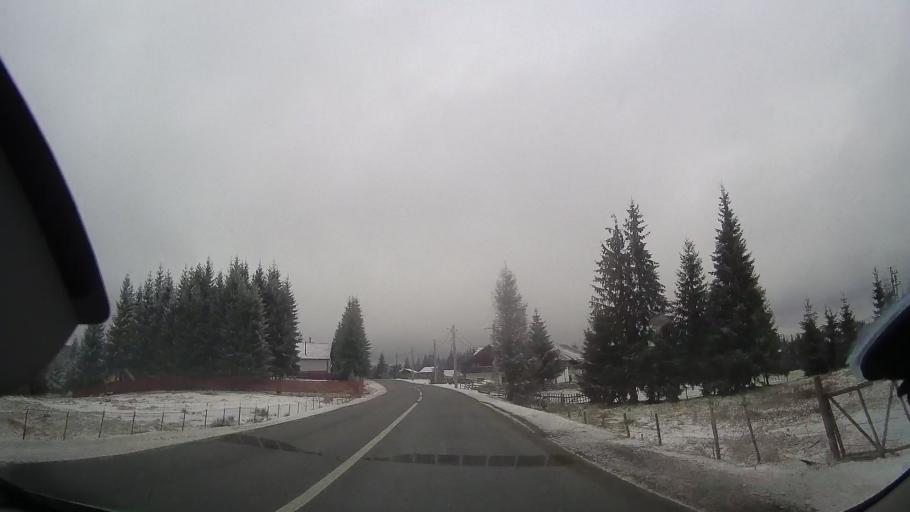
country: RO
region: Cluj
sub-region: Comuna Belis
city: Belis
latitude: 46.6797
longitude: 23.0413
